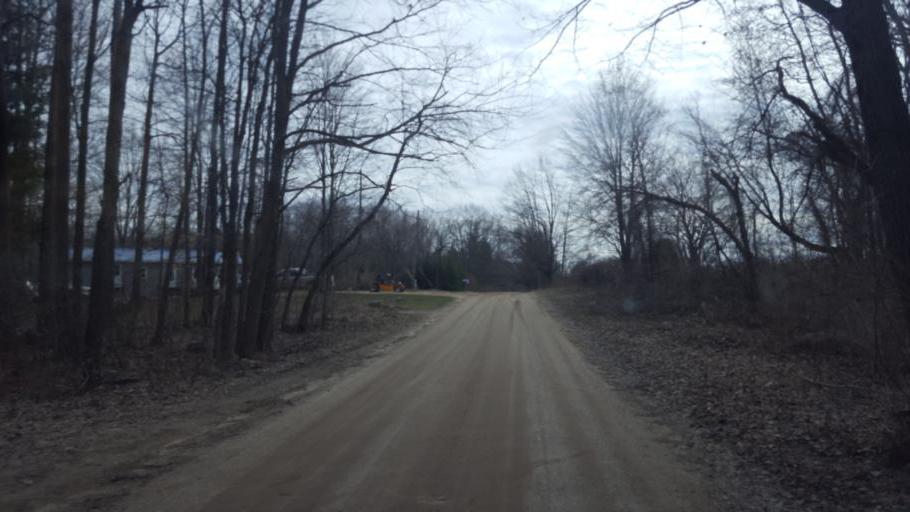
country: US
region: Michigan
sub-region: Isabella County
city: Lake Isabella
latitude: 43.6694
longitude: -85.1266
